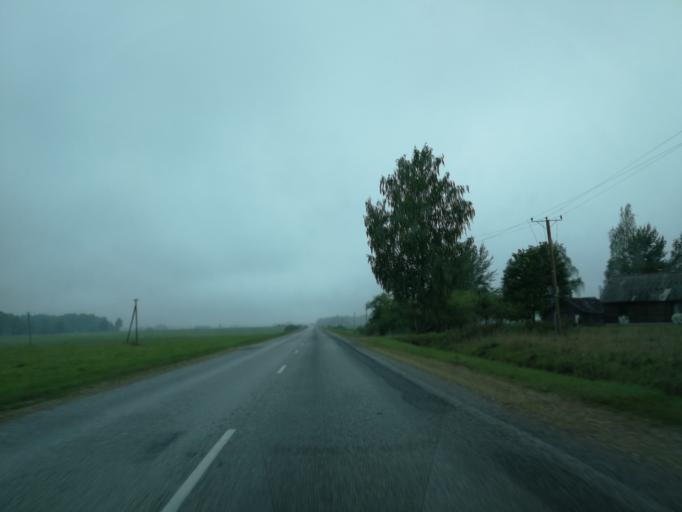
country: LV
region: Preilu Rajons
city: Preili
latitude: 56.3049
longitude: 26.6172
